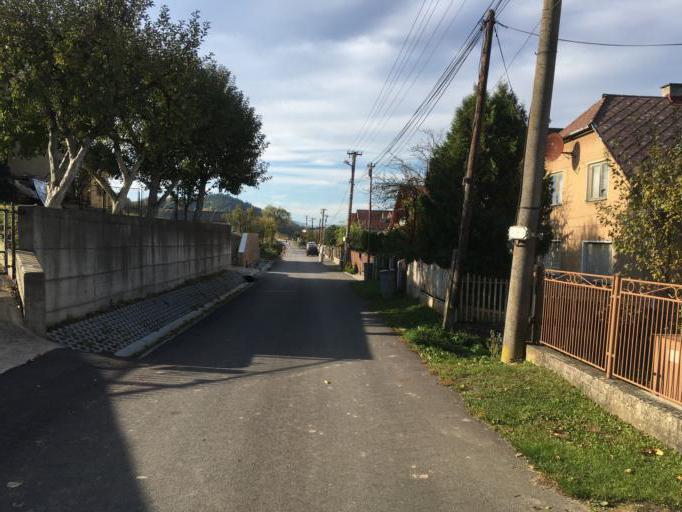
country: SK
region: Trenciansky
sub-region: Okres Povazska Bystrica
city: Povazska Bystrica
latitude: 49.0527
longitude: 18.4057
